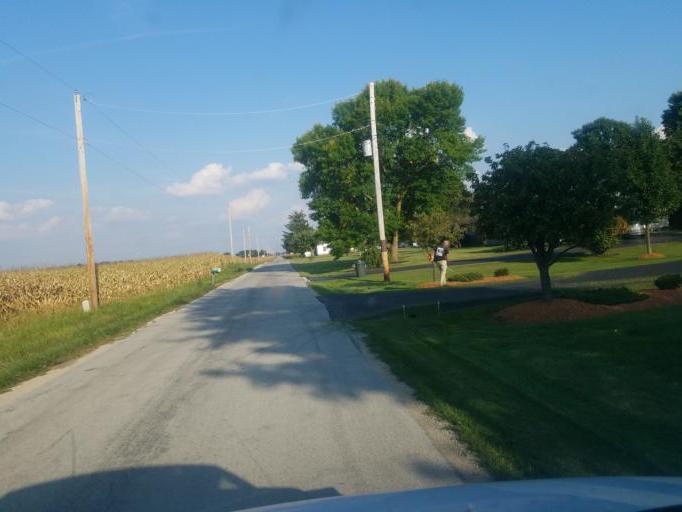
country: US
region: Ohio
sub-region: Wyandot County
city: Upper Sandusky
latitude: 40.9352
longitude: -83.1717
